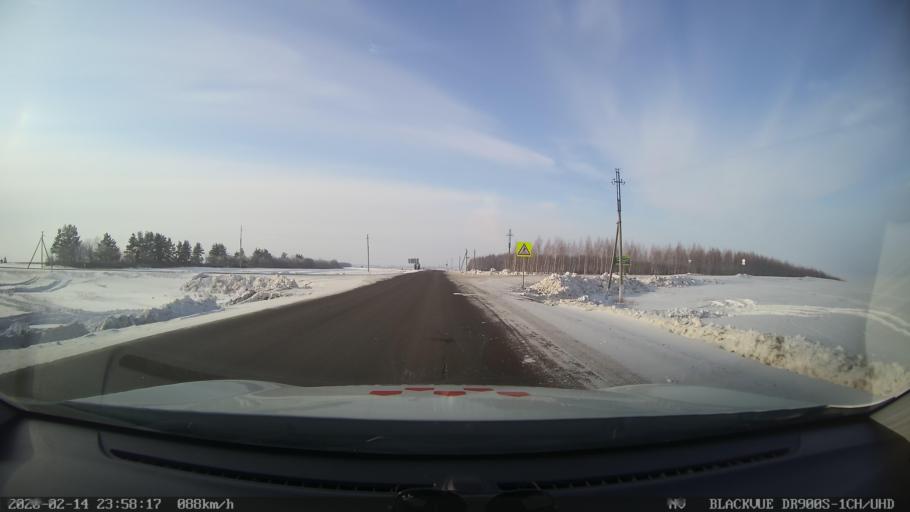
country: RU
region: Tatarstan
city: Kuybyshevskiy Zaton
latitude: 55.3399
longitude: 49.0906
